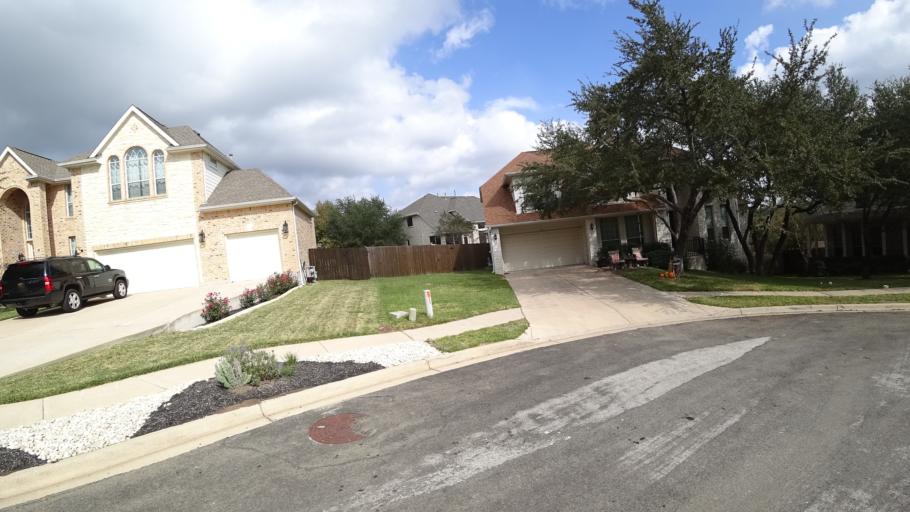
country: US
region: Texas
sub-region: Williamson County
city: Anderson Mill
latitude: 30.4229
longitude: -97.8593
